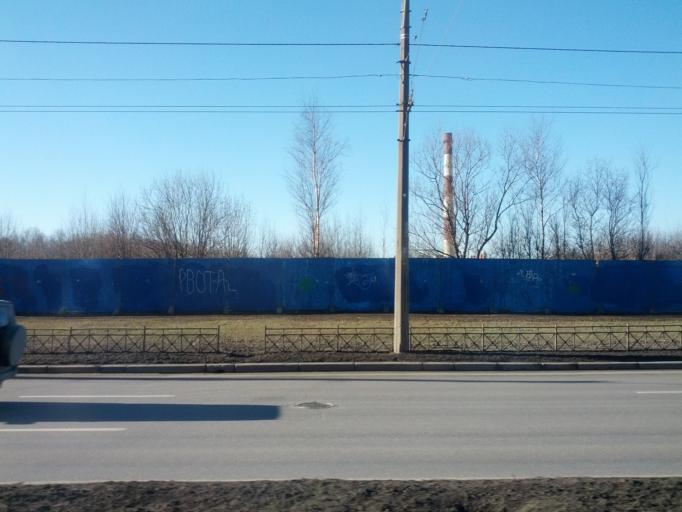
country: RU
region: St.-Petersburg
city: Centralniy
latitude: 59.9161
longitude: 30.4311
